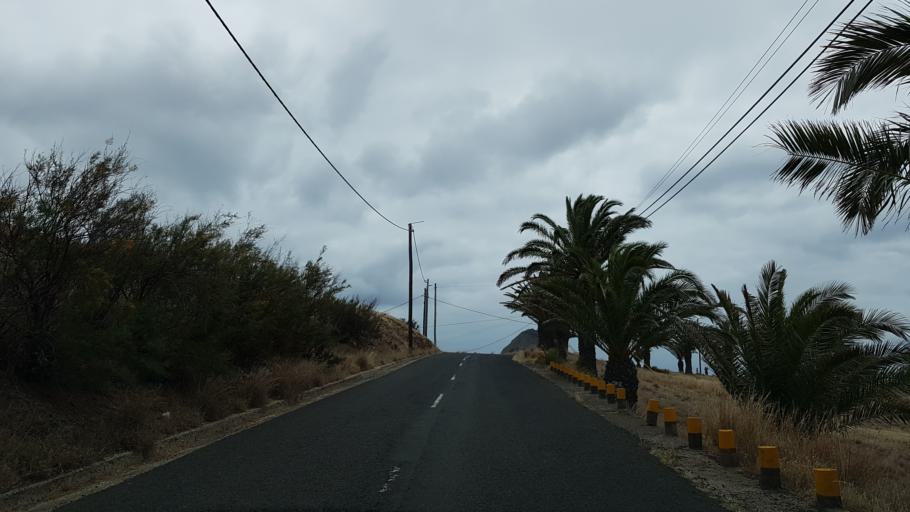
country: PT
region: Madeira
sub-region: Porto Santo
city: Vila de Porto Santo
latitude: 33.0686
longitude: -16.3187
